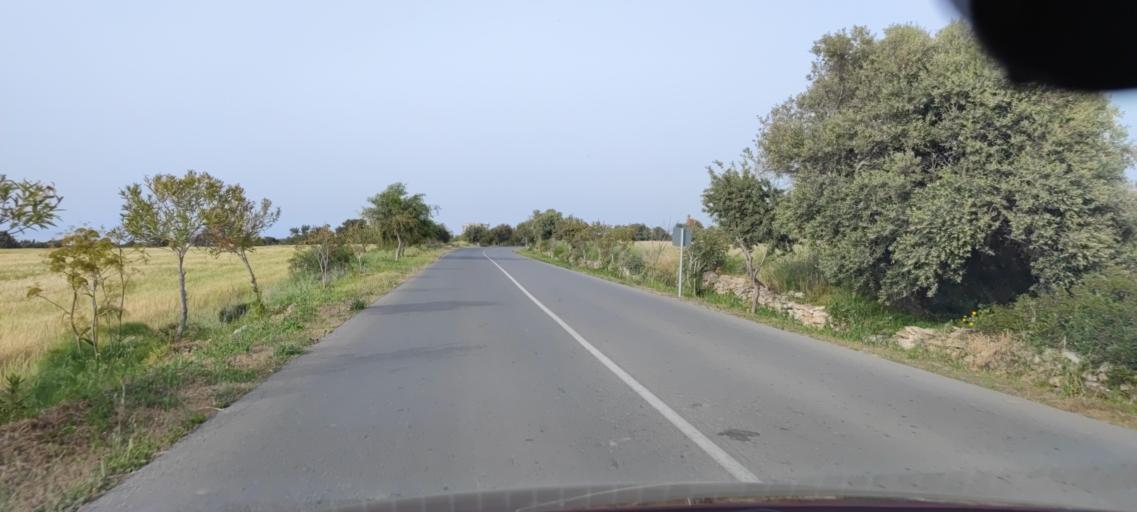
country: CY
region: Ammochostos
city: Leonarisso
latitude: 35.5431
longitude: 34.1978
